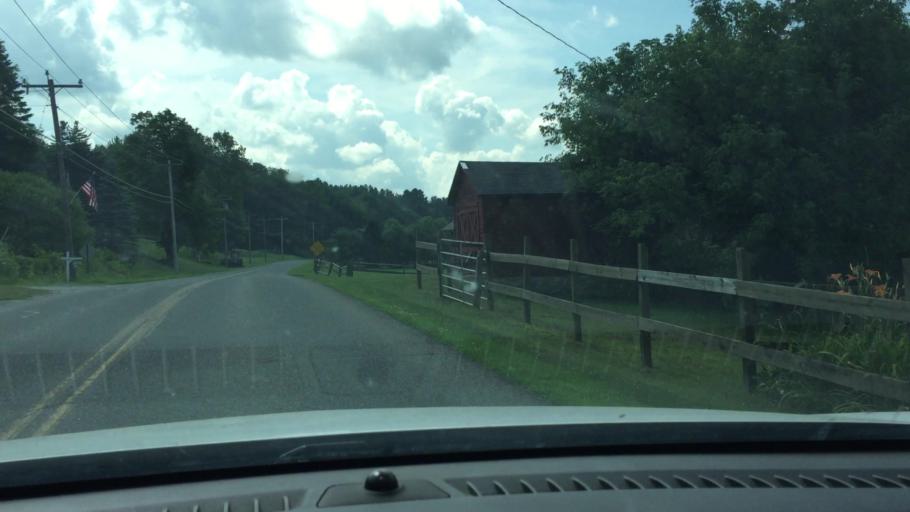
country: US
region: Massachusetts
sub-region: Berkshire County
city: Lee
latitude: 42.2403
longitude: -73.1965
